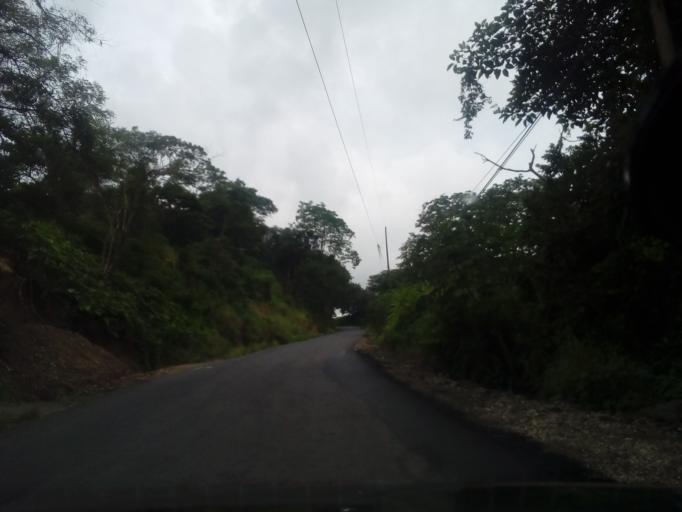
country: CR
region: Guanacaste
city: Samara
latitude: 9.9202
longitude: -85.5286
